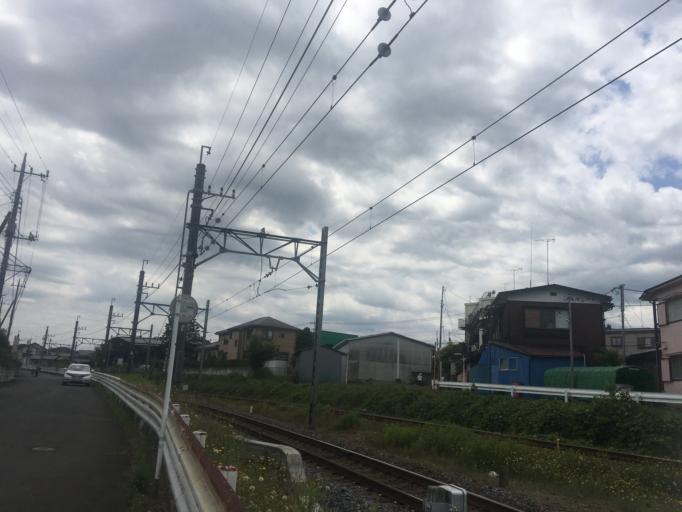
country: JP
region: Saitama
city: Morohongo
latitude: 35.9610
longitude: 139.3000
